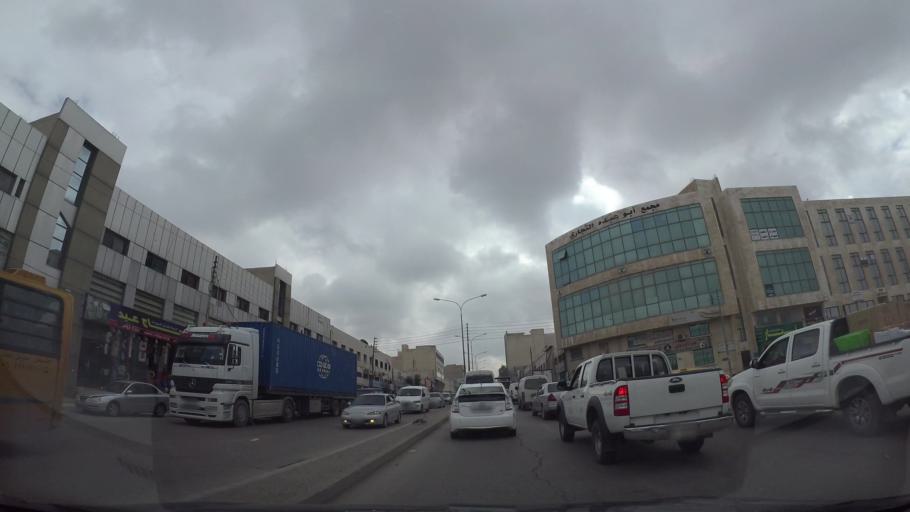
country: JO
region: Amman
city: Al Quwaysimah
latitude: 31.9121
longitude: 35.9388
